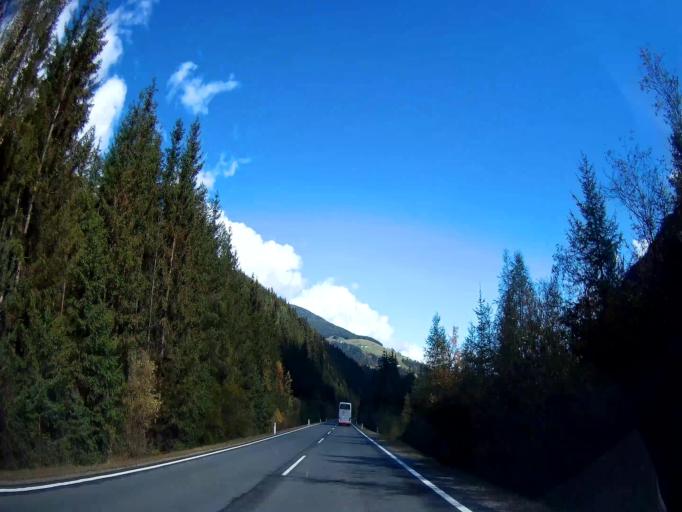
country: AT
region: Tyrol
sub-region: Politischer Bezirk Lienz
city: Anras
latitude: 46.7619
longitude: 12.5630
